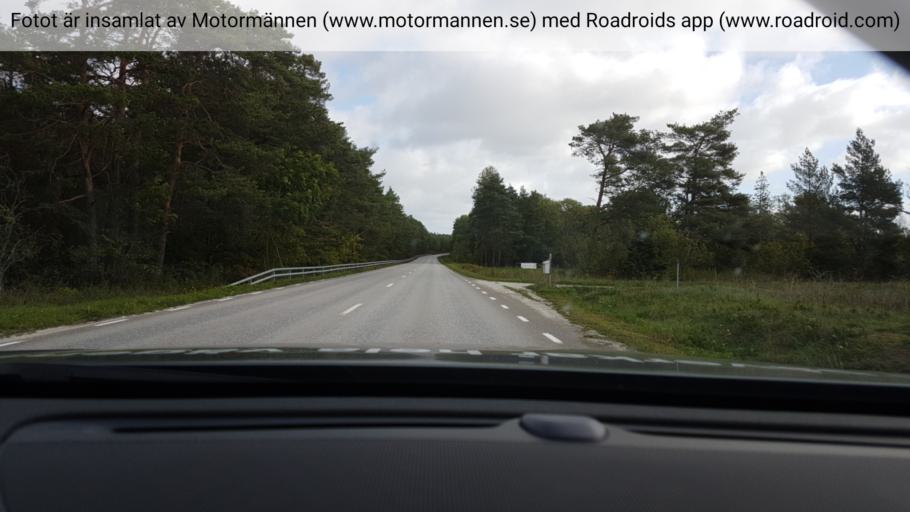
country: SE
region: Gotland
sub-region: Gotland
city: Slite
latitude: 57.8522
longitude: 18.9831
